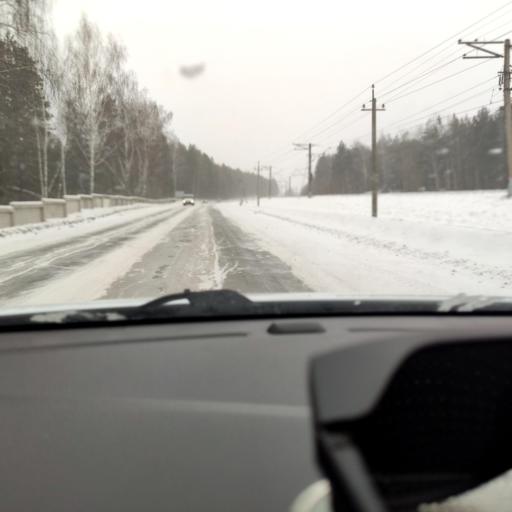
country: RU
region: Tatarstan
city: Vysokaya Gora
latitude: 55.8936
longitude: 49.2516
